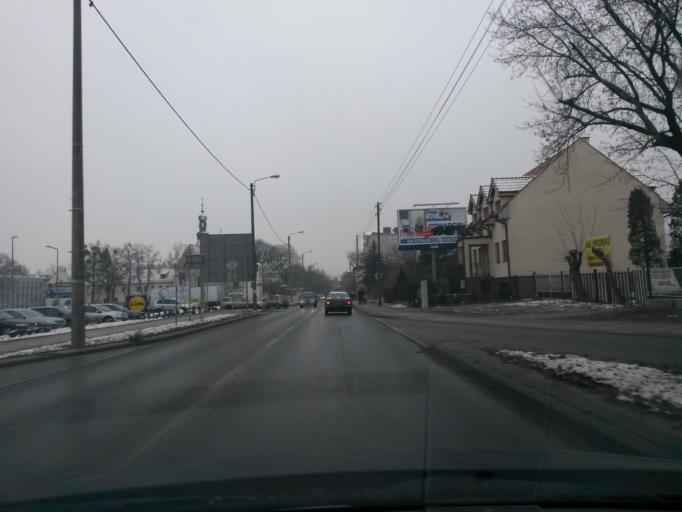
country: PL
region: Kujawsko-Pomorskie
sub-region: Torun
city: Torun
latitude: 52.9951
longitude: 18.6003
